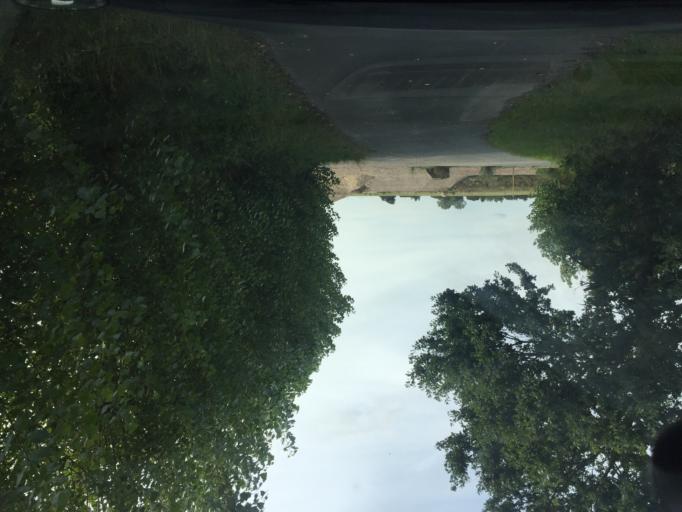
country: DK
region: South Denmark
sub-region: Kerteminde Kommune
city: Langeskov
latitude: 55.3467
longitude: 10.5184
